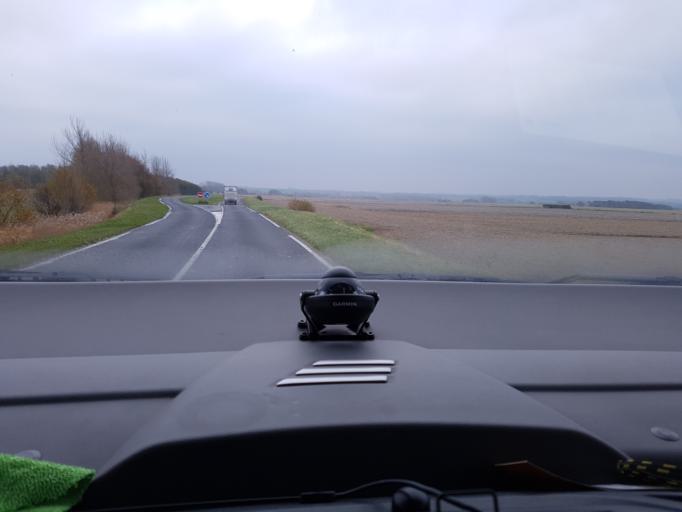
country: FR
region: Picardie
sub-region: Departement de la Somme
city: Cayeux-sur-Mer
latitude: 50.1546
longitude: 1.4987
